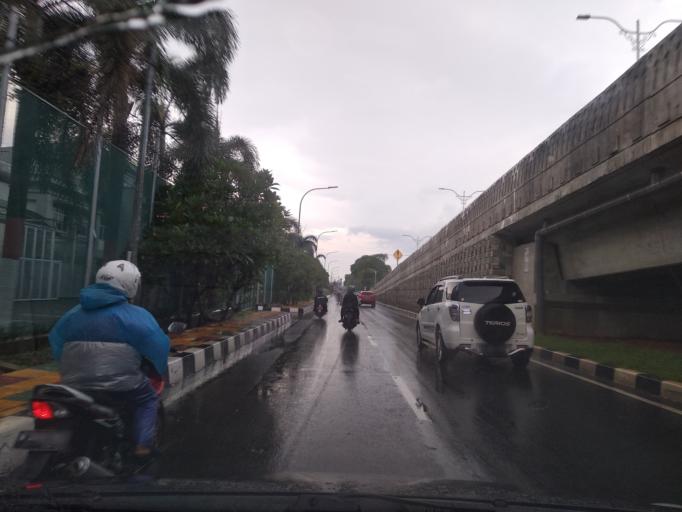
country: ID
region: Jakarta Raya
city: Jakarta
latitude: -6.2145
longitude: 106.8863
